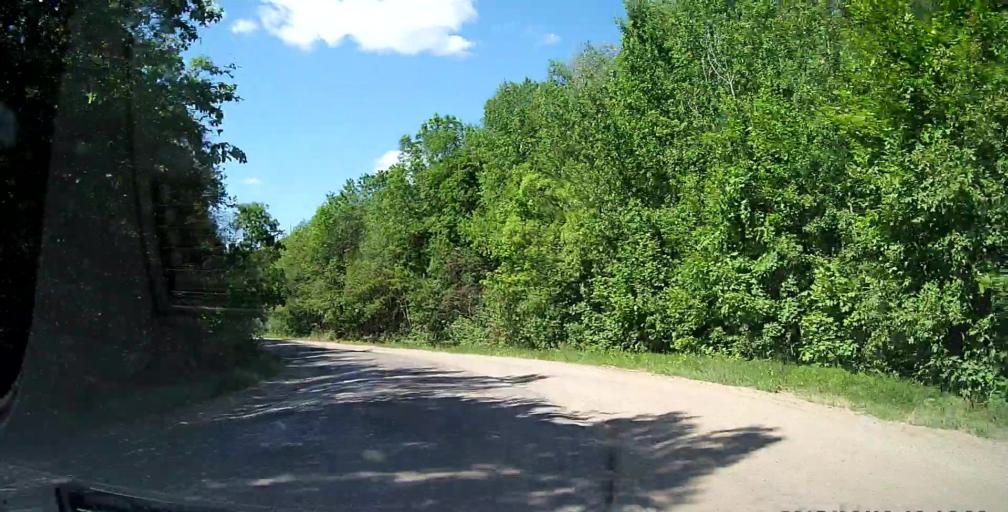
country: RU
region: Tula
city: Kurkino
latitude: 53.1930
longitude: 38.5220
